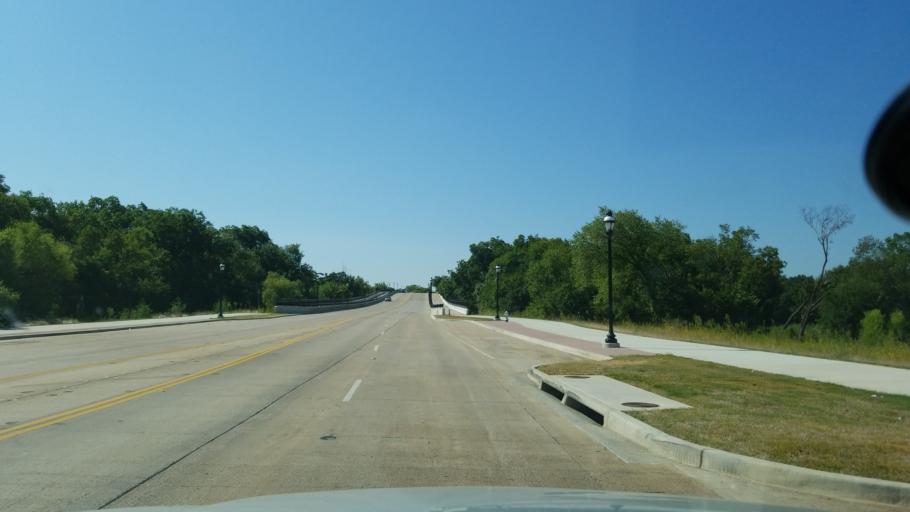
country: US
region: Texas
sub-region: Tarrant County
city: Mansfield
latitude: 32.5707
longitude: -97.1429
